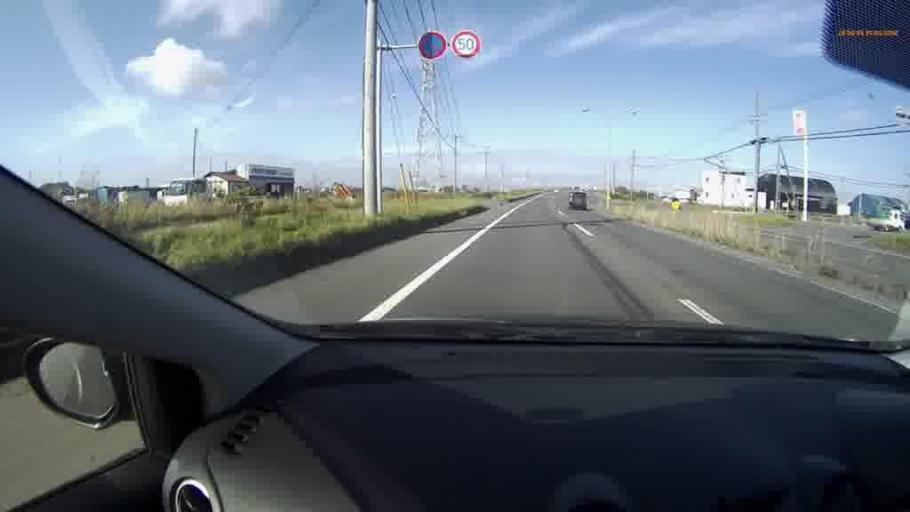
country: JP
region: Hokkaido
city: Kushiro
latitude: 42.9985
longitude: 144.4265
